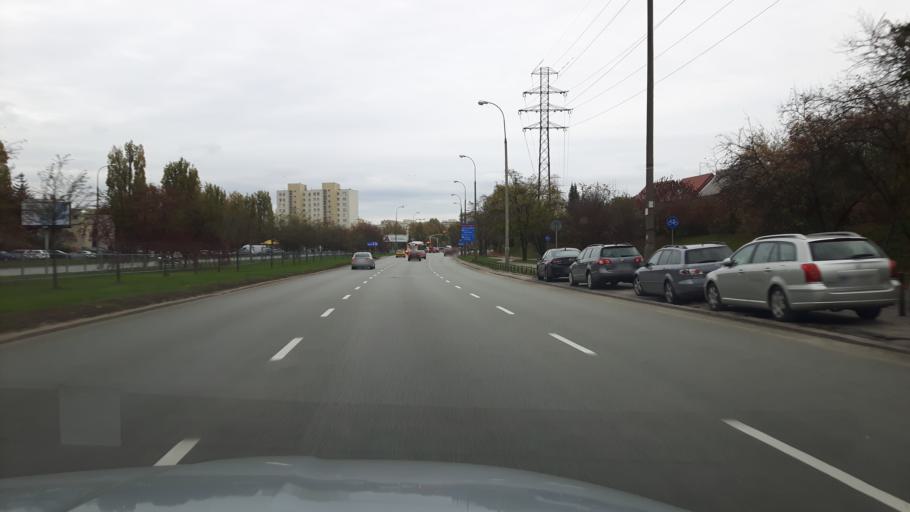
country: PL
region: Masovian Voivodeship
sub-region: Warszawa
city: Ursynow
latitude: 52.1505
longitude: 21.0288
